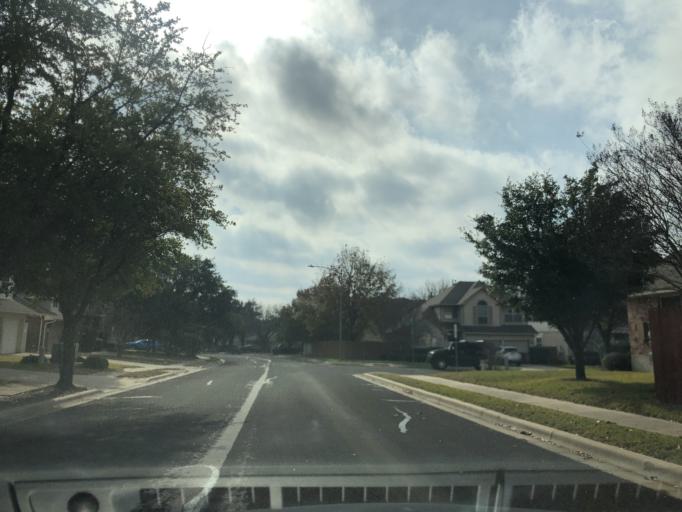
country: US
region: Texas
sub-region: Travis County
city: Wells Branch
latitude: 30.4256
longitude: -97.6817
